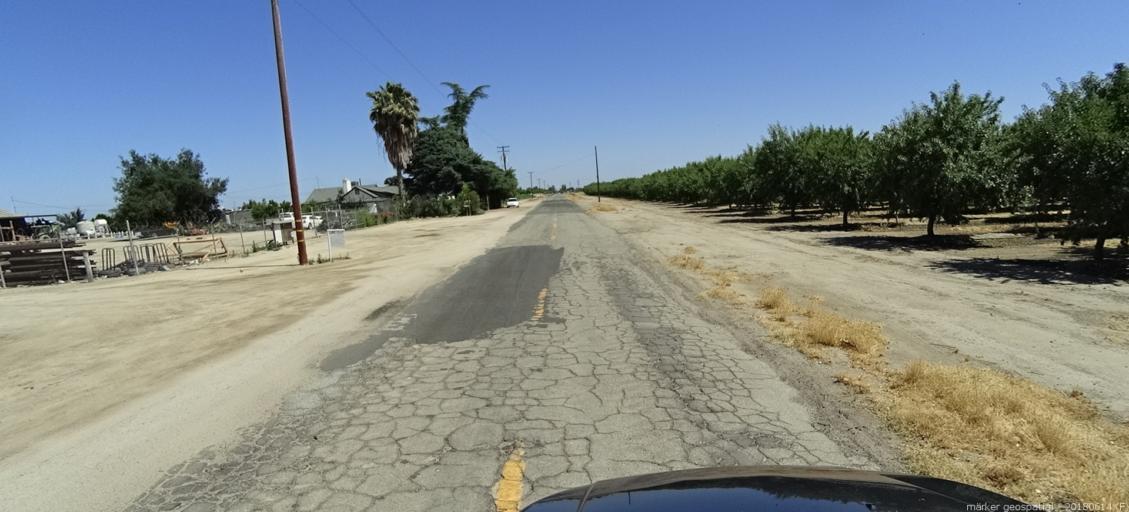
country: US
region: California
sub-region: Madera County
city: Fairmead
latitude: 36.9781
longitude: -120.1842
